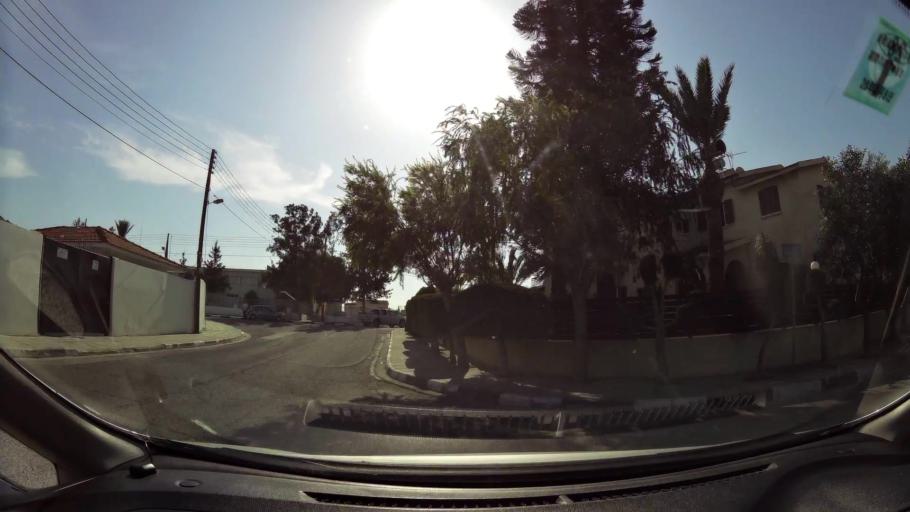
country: CY
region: Larnaka
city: Aradippou
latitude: 34.9479
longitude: 33.5879
